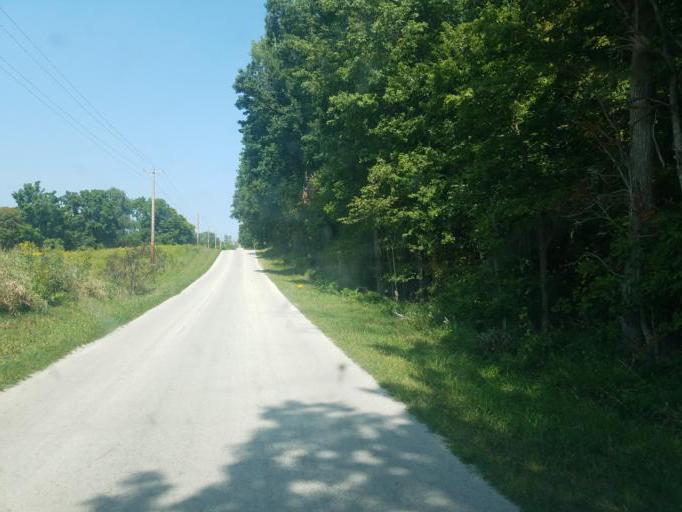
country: US
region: Ohio
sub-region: Crawford County
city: Bucyrus
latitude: 40.8276
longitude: -83.1123
